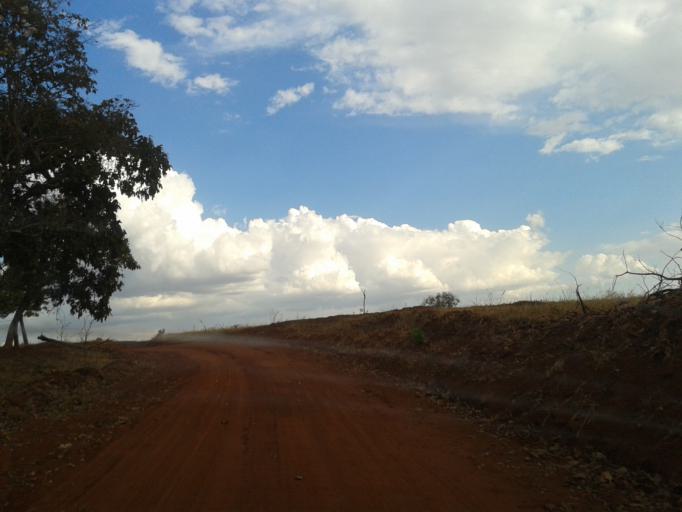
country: BR
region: Minas Gerais
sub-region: Santa Vitoria
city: Santa Vitoria
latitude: -19.1814
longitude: -49.9451
